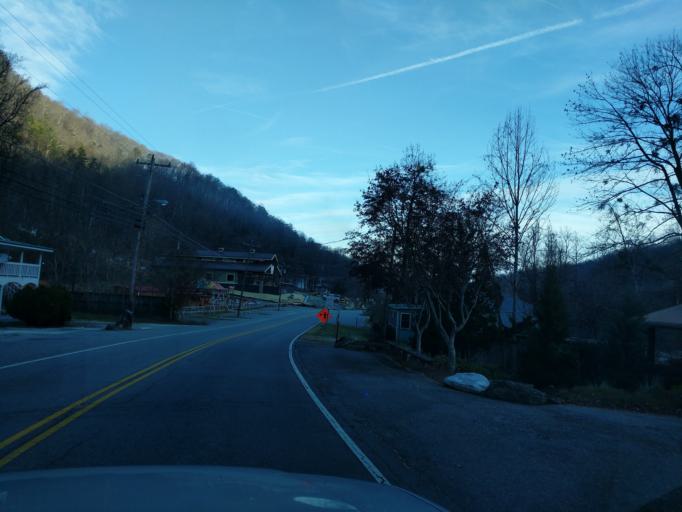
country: US
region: North Carolina
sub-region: Rutherford County
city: Lake Lure
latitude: 35.4409
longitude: -82.2516
